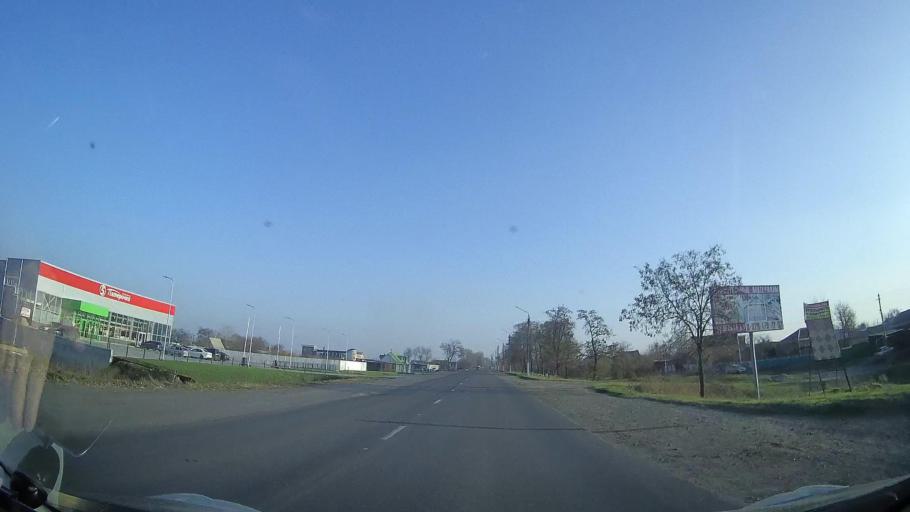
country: RU
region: Rostov
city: Ol'ginskaya
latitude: 47.1998
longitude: 39.9344
